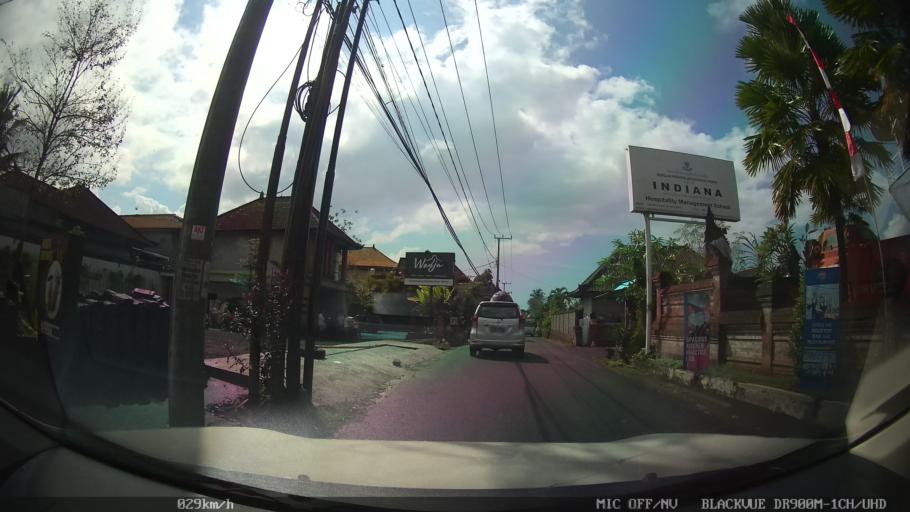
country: ID
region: Bali
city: Banjar Tebongkang
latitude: -8.5418
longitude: 115.2688
